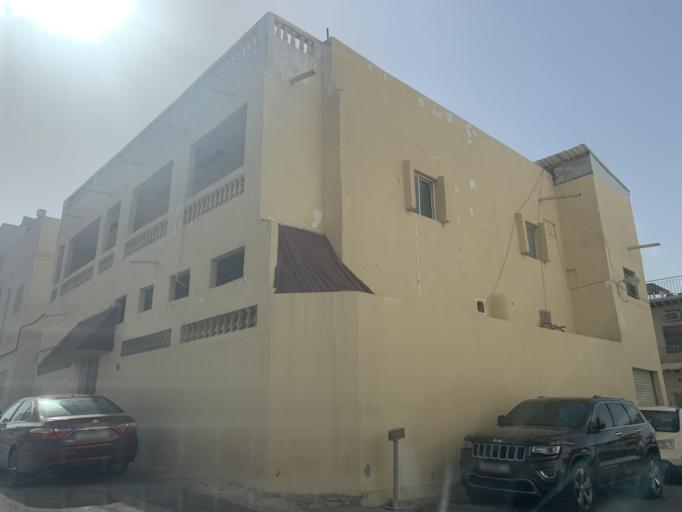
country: BH
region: Manama
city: Jidd Hafs
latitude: 26.2066
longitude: 50.5481
